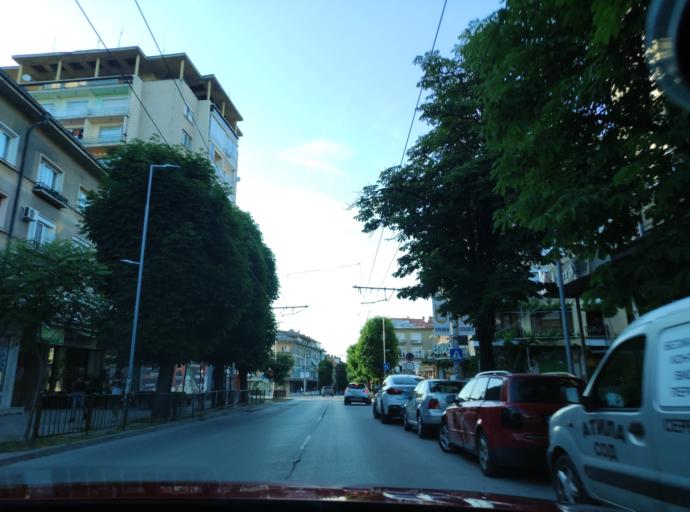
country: BG
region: Pleven
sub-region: Obshtina Pleven
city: Pleven
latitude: 43.4026
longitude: 24.6212
